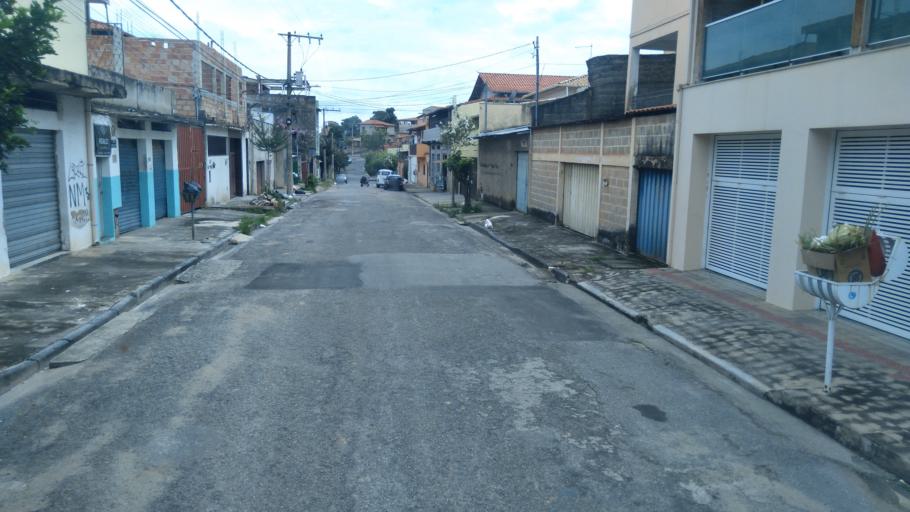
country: BR
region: Minas Gerais
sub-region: Belo Horizonte
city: Belo Horizonte
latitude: -19.8500
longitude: -43.9063
